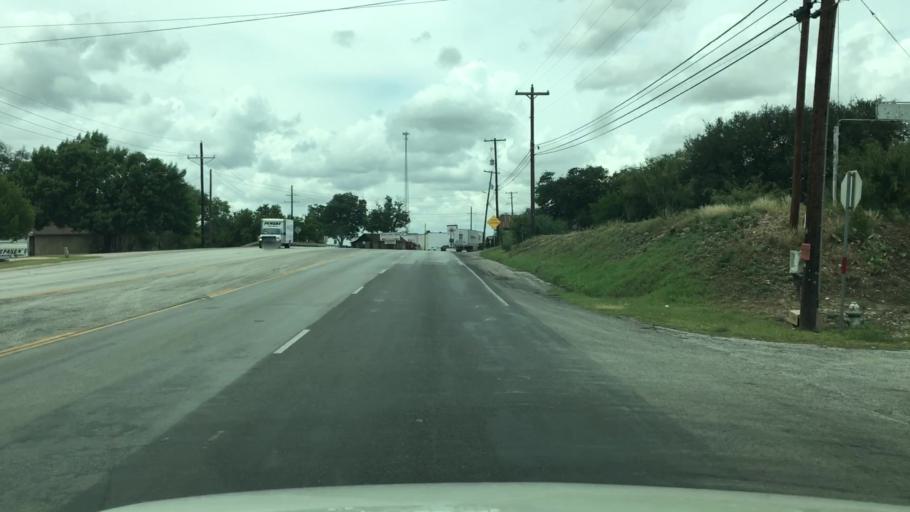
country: US
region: Texas
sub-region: McCulloch County
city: Brady
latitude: 31.1365
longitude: -99.3441
